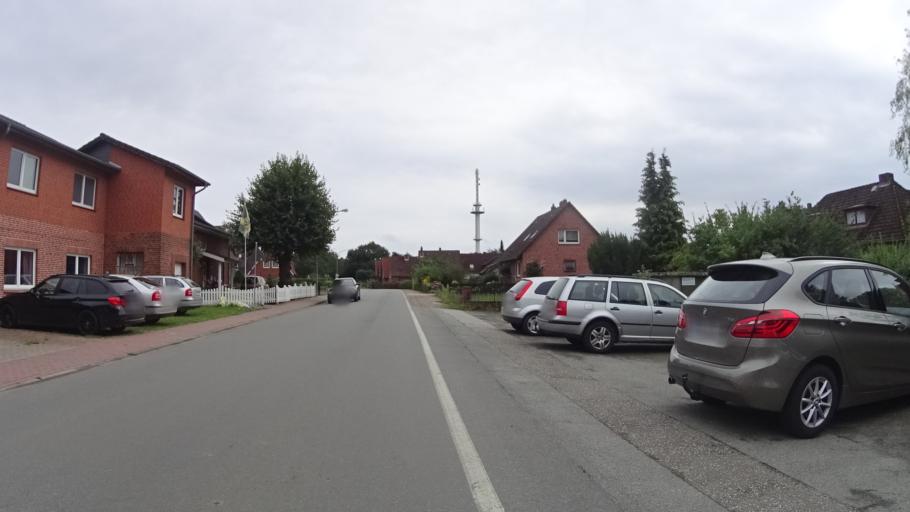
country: DE
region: Schleswig-Holstein
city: Steinhorst
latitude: 53.7172
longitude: 10.4853
